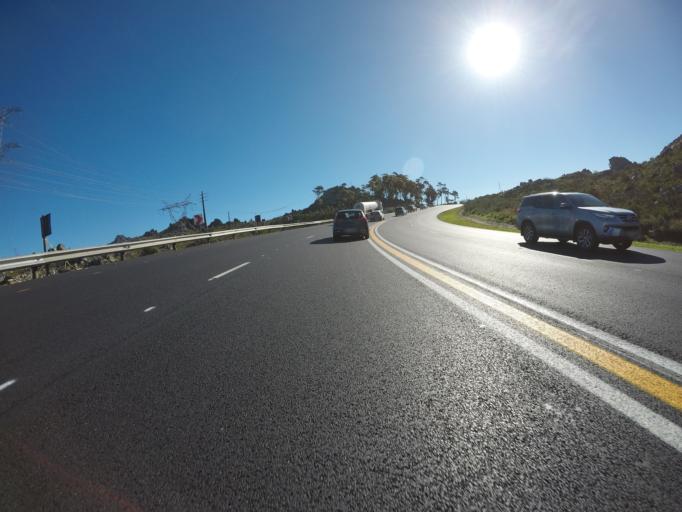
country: ZA
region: Western Cape
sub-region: Overberg District Municipality
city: Grabouw
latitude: -34.1510
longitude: 18.9294
